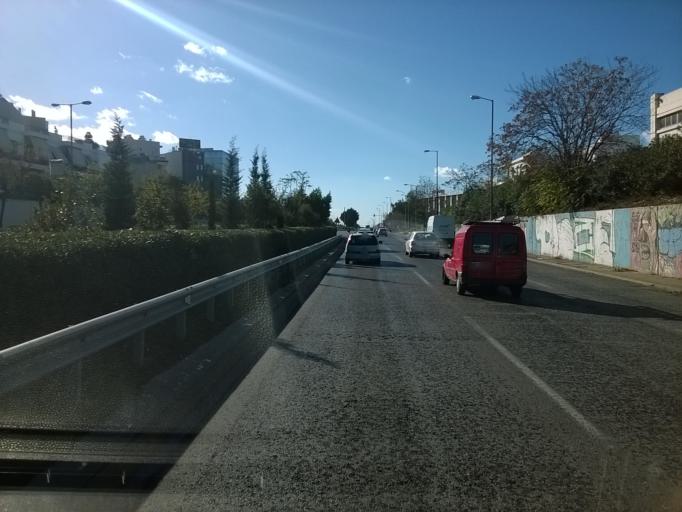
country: GR
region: Attica
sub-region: Nomarchia Athinas
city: Agios Dimitrios
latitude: 37.9260
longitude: 23.7443
